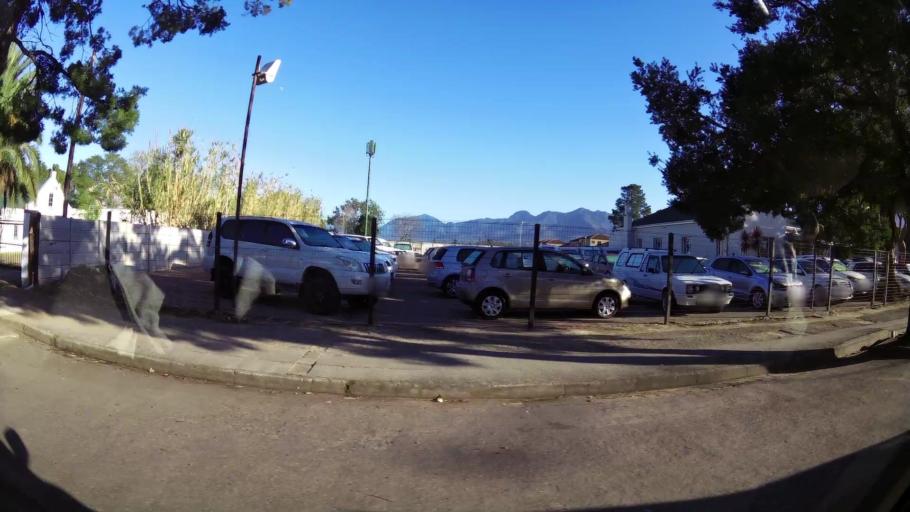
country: ZA
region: Western Cape
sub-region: Eden District Municipality
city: George
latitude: -33.9672
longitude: 22.4500
